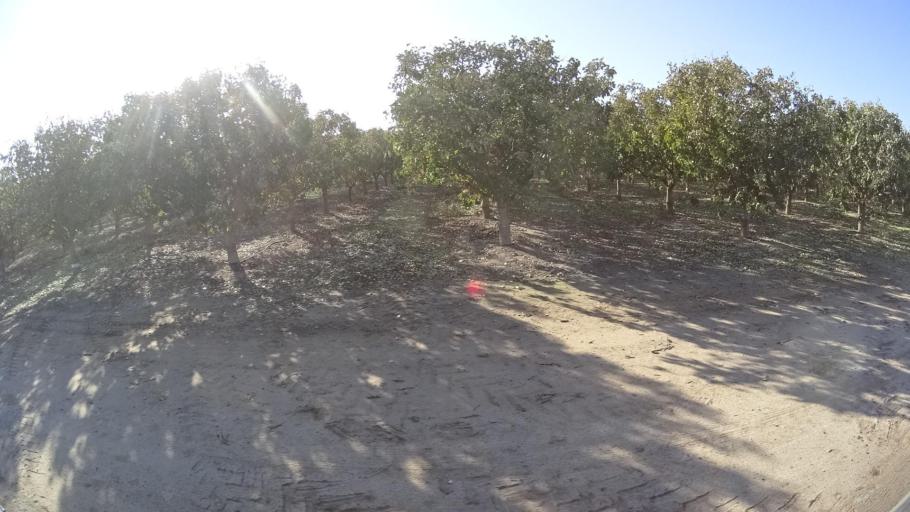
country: US
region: California
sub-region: Tulare County
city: Richgrove
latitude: 35.7327
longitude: -119.1154
